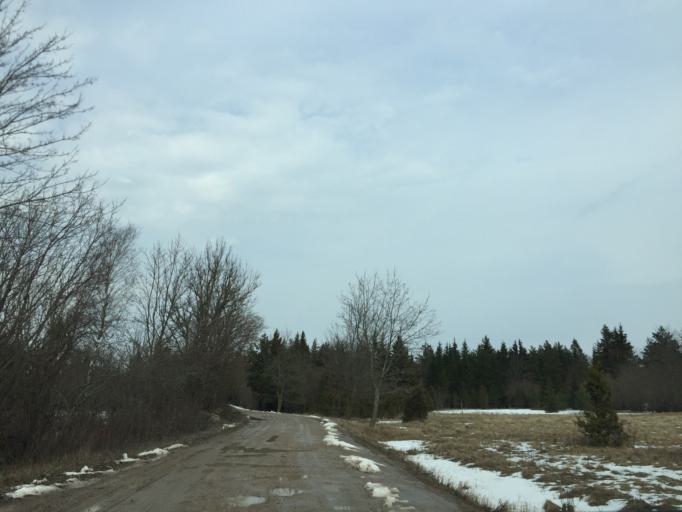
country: EE
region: Saare
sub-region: Kuressaare linn
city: Kuressaare
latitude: 58.4229
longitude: 22.1515
